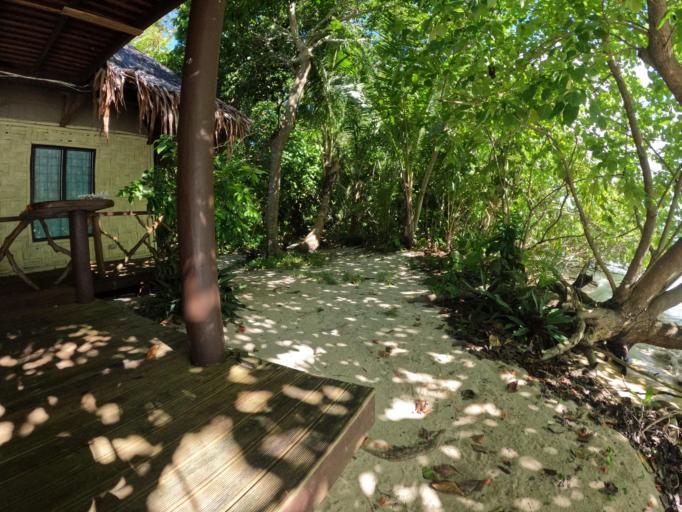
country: FJ
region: Central
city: Suva
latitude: -17.8091
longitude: 178.7213
